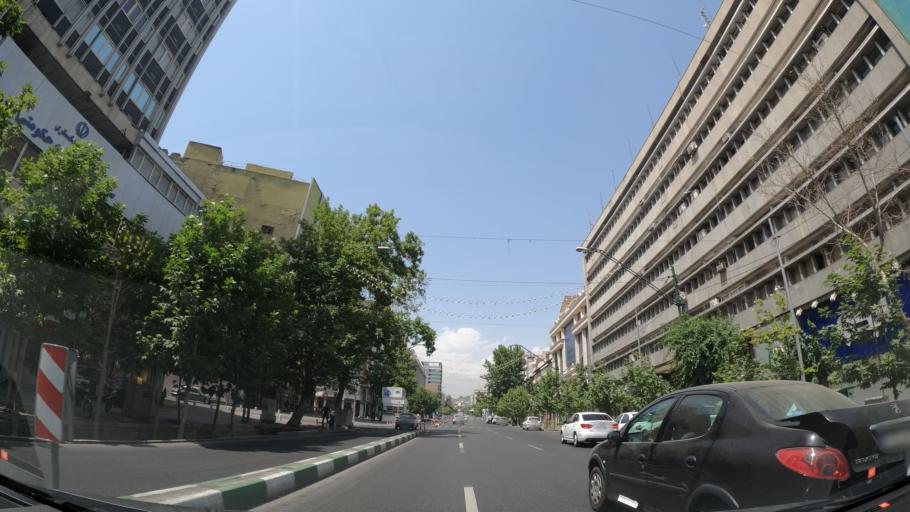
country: IR
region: Tehran
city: Tehran
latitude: 35.7182
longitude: 51.4133
